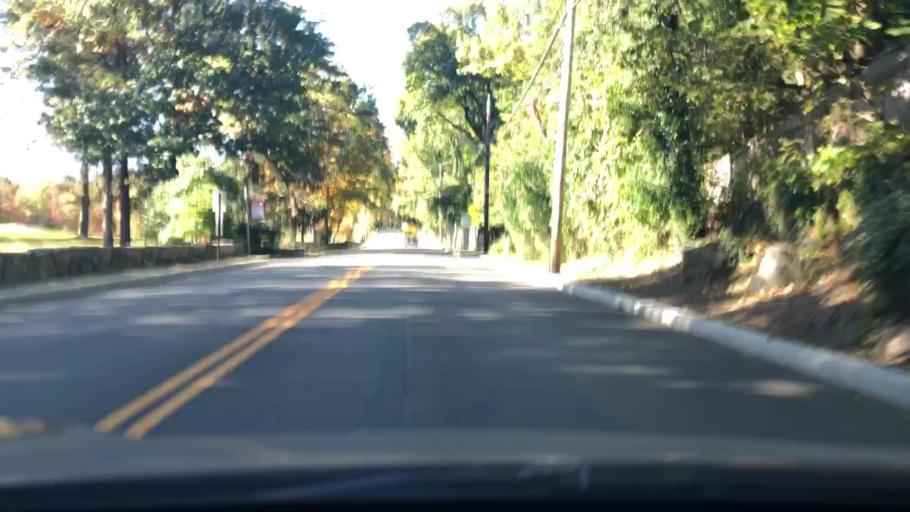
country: US
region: New York
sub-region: Westchester County
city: Harrison
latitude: 40.9807
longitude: -73.7014
